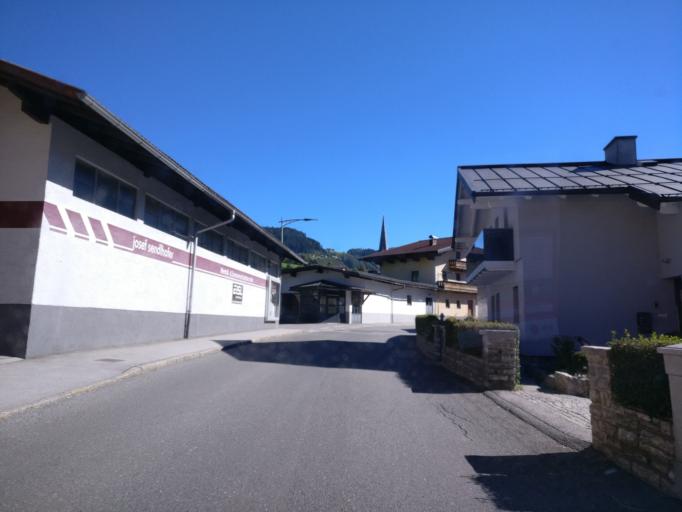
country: AT
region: Salzburg
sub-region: Politischer Bezirk Sankt Johann im Pongau
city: Pfarrwerfen
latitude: 47.4601
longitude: 13.2028
